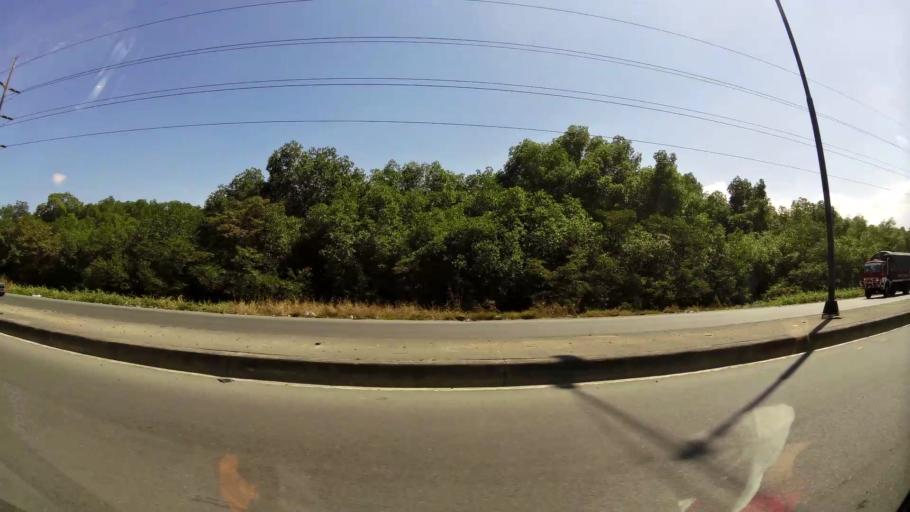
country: EC
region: Guayas
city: Guayaquil
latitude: -2.2169
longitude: -79.9566
